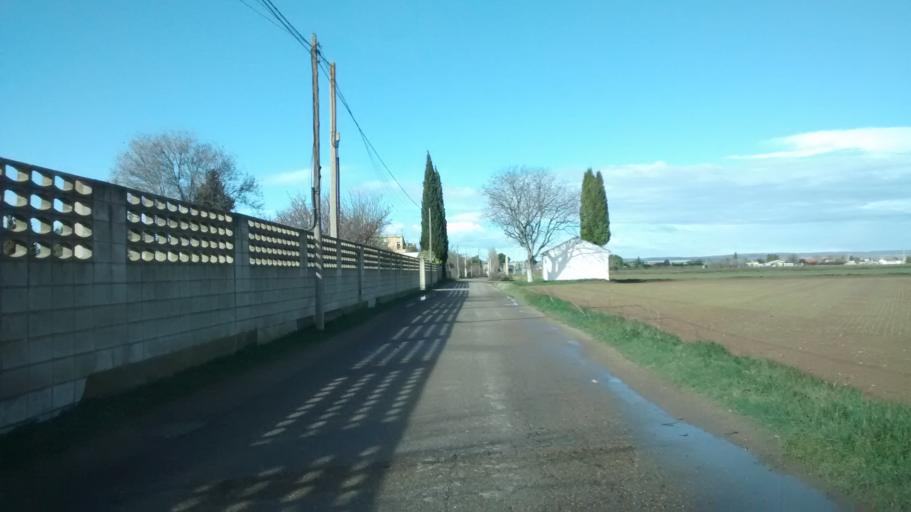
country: ES
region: Aragon
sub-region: Provincia de Zaragoza
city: Villanueva de Gallego
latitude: 41.7294
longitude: -0.7876
